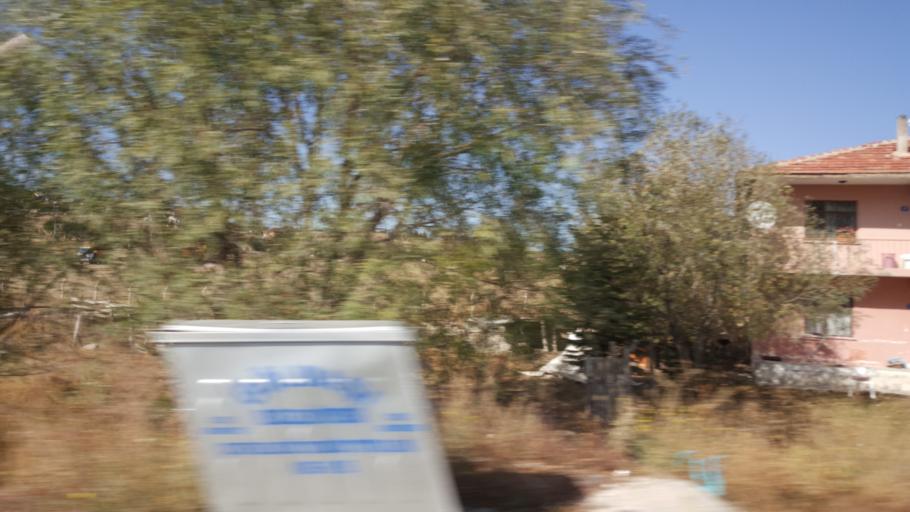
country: TR
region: Ankara
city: Ikizce
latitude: 39.6597
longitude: 32.7319
